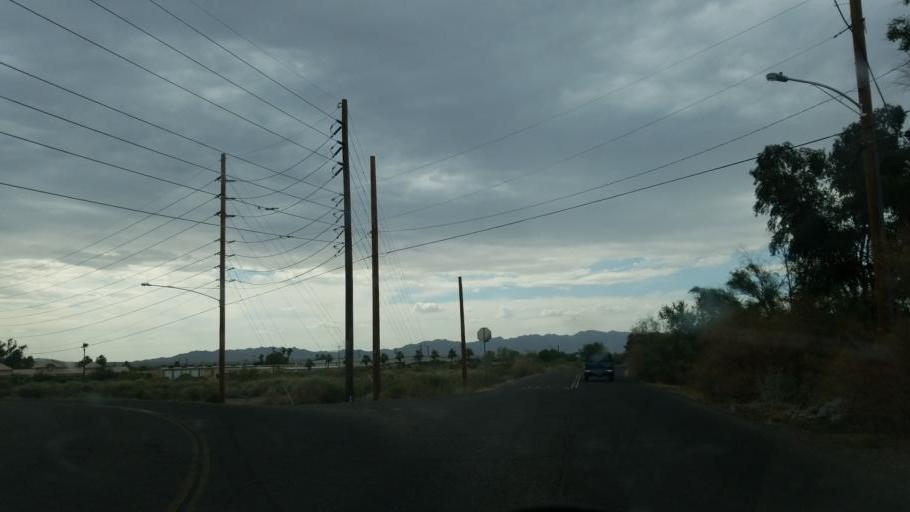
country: US
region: California
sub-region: San Bernardino County
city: Needles
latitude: 34.8483
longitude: -114.6078
